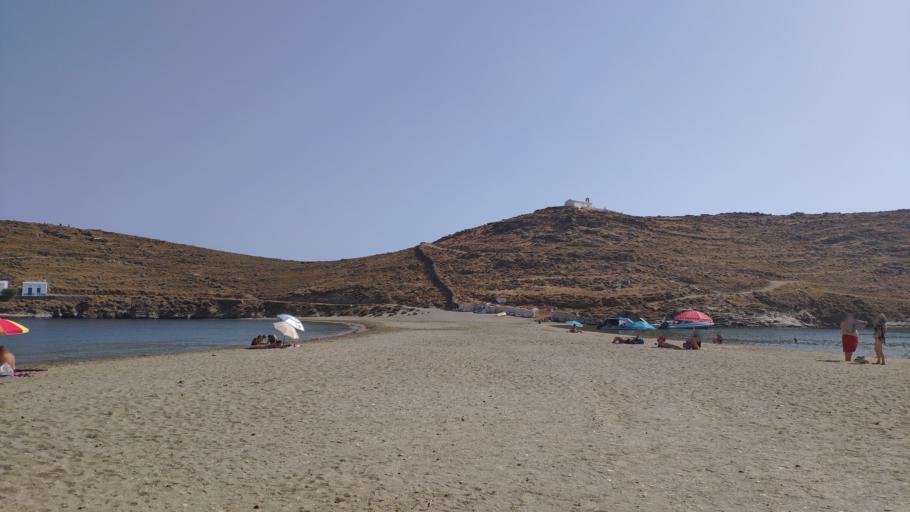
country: GR
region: South Aegean
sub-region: Nomos Kykladon
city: Kythnos
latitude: 37.4148
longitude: 24.3792
